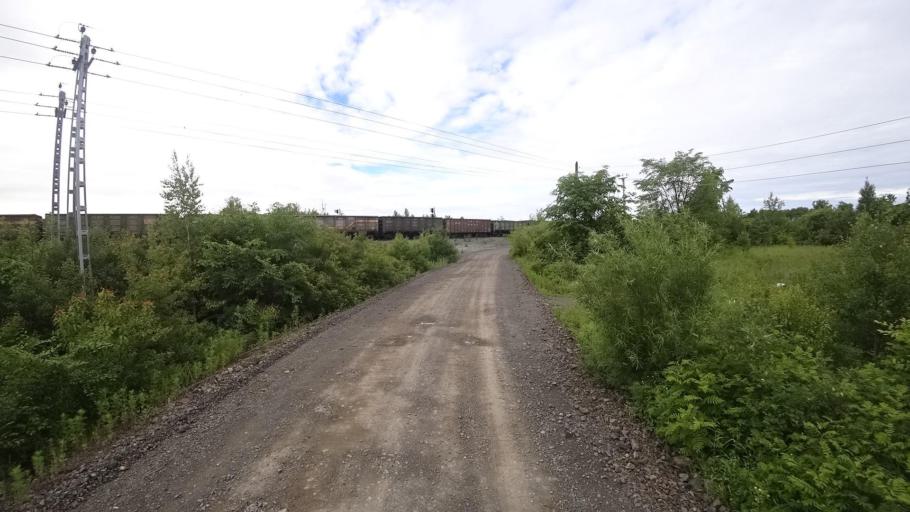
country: RU
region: Khabarovsk Krai
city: Amursk
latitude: 49.8953
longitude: 136.1282
